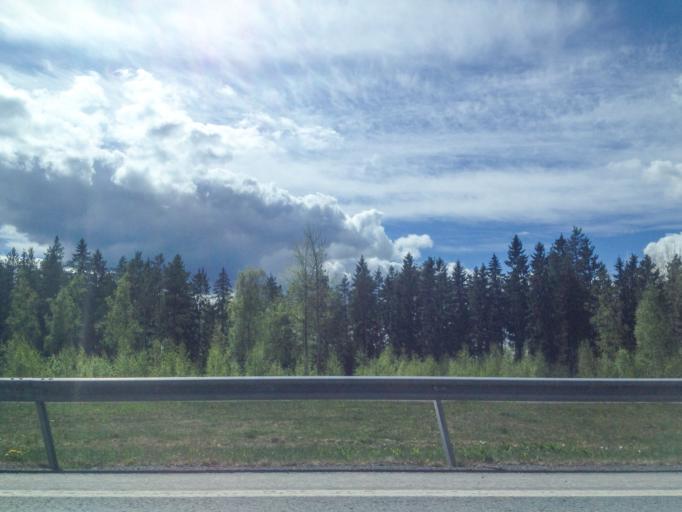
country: FI
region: Pirkanmaa
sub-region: Etelae-Pirkanmaa
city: Viiala
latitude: 61.2717
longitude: 23.8176
